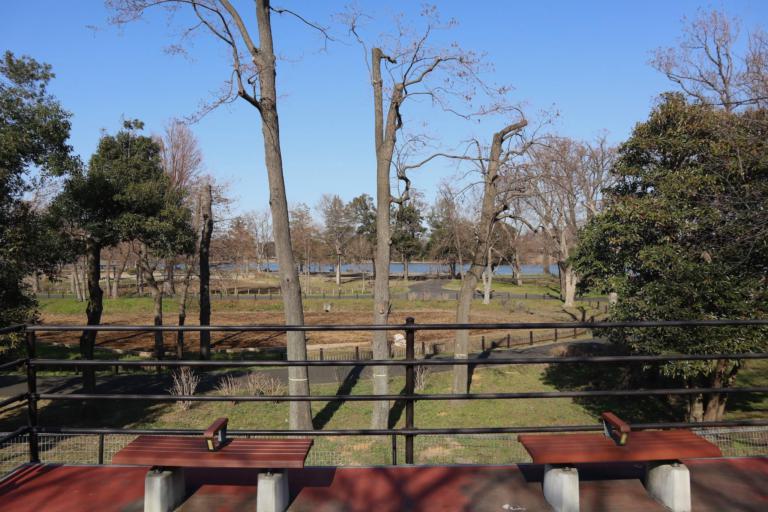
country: JP
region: Chiba
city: Matsudo
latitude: 35.7801
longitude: 139.8725
